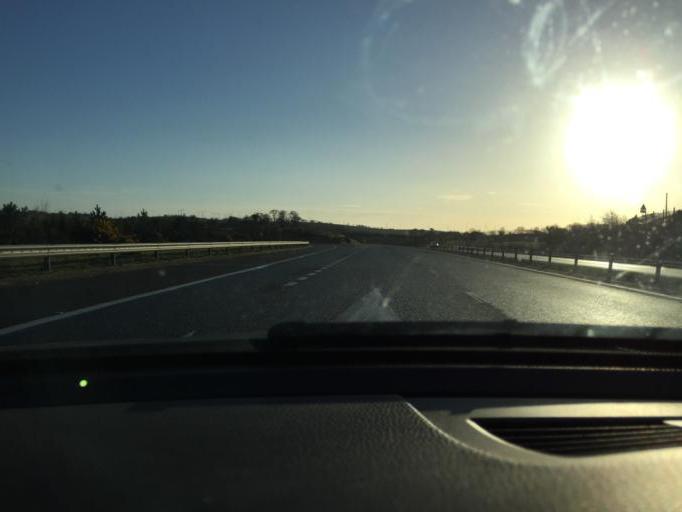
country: GB
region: Northern Ireland
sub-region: Newry and Mourne District
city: Newry
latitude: 54.2152
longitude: -6.3364
